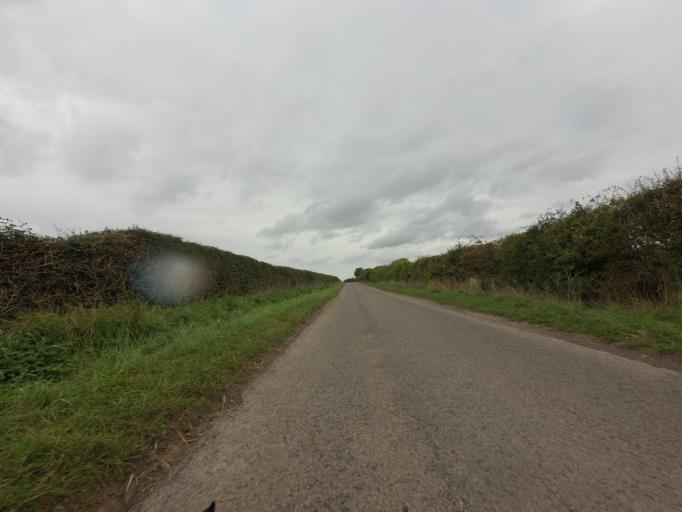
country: GB
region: England
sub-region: Cambridgeshire
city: Duxford
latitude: 52.0588
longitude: 0.1216
